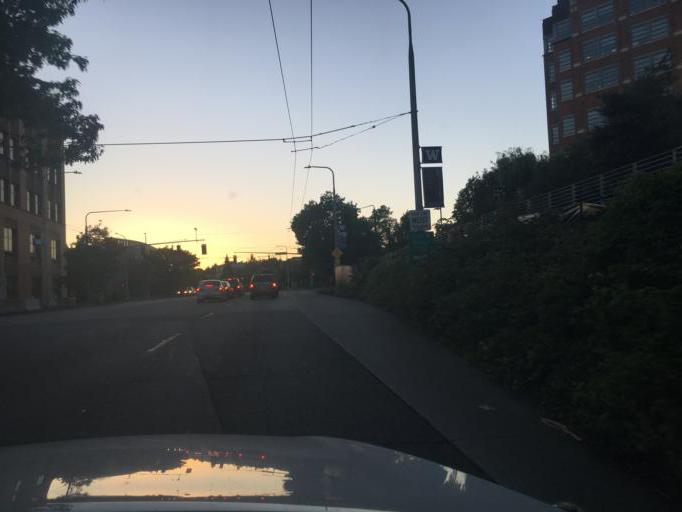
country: US
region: Washington
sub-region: King County
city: Seattle
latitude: 47.6525
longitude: -122.3116
